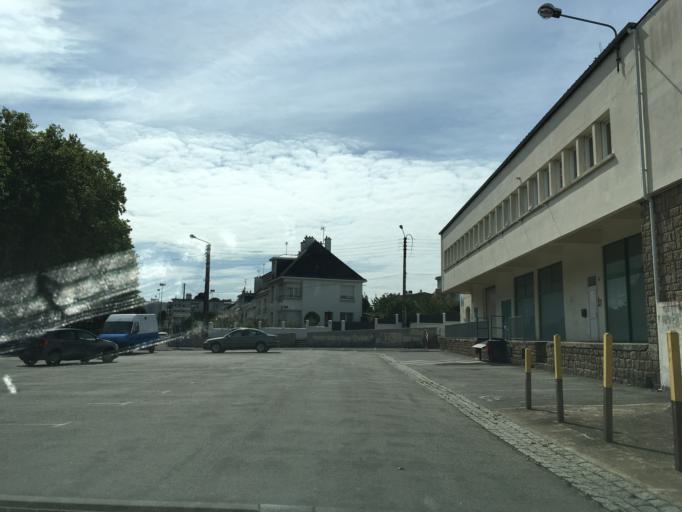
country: FR
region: Brittany
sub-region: Departement du Morbihan
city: Lorient
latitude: 47.7532
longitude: -3.3749
